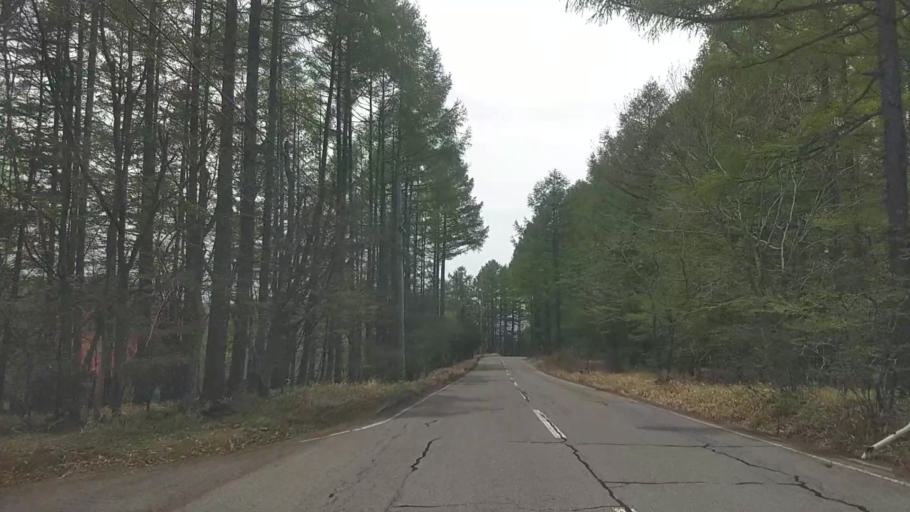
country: JP
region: Nagano
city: Chino
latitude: 36.0469
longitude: 138.3054
